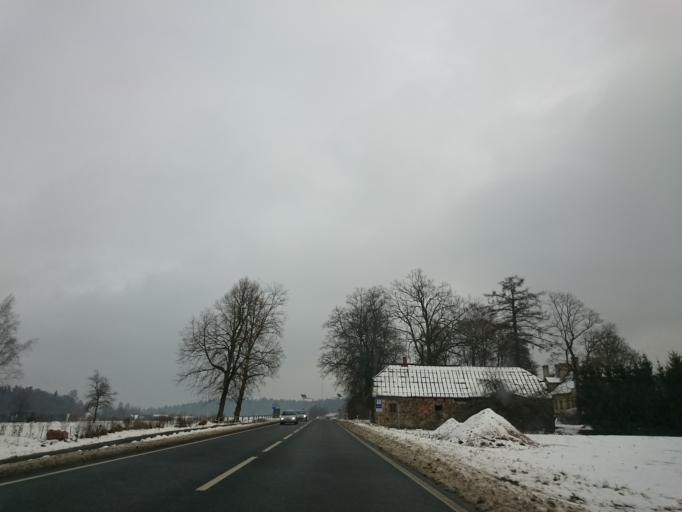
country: LV
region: Pargaujas
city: Stalbe
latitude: 57.3544
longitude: 24.9574
